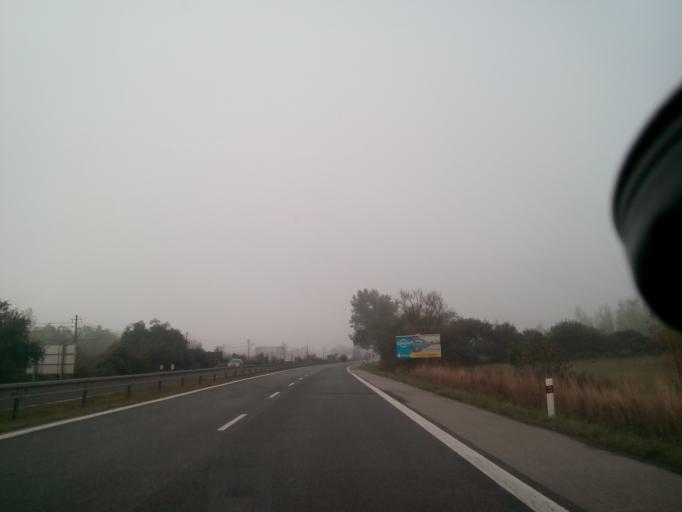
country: SK
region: Kosicky
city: Kosice
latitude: 48.6487
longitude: 21.2036
